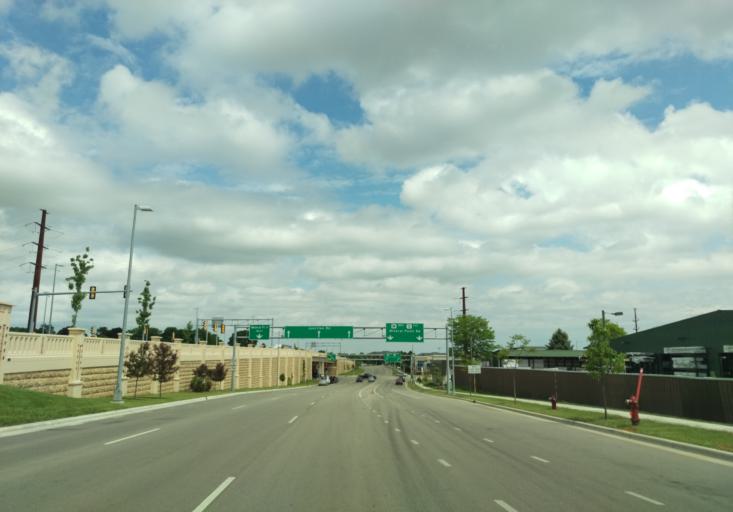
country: US
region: Wisconsin
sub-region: Dane County
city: Middleton
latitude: 43.0587
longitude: -89.5275
